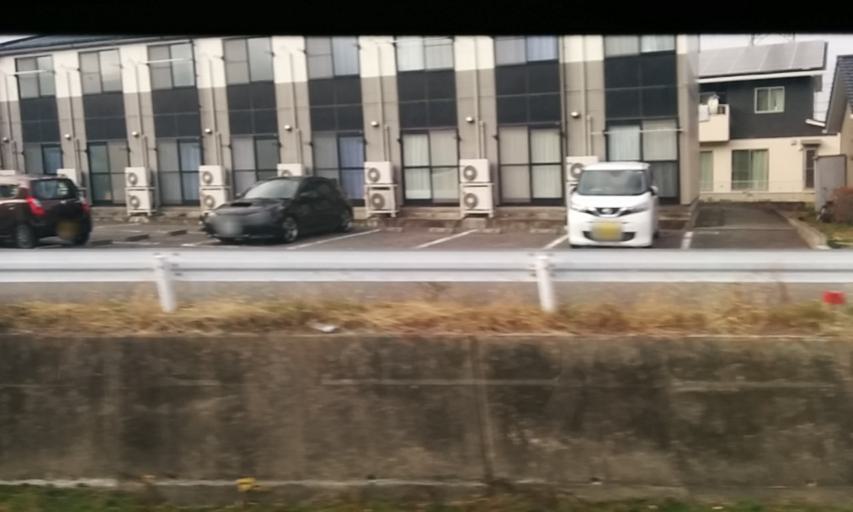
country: JP
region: Nagano
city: Shiojiri
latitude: 36.1114
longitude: 137.9457
